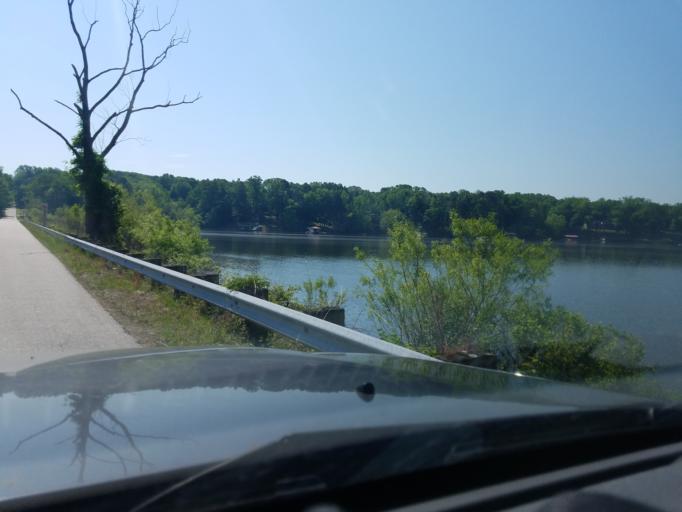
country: US
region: North Carolina
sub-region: Vance County
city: Henderson
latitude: 36.4092
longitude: -78.3937
